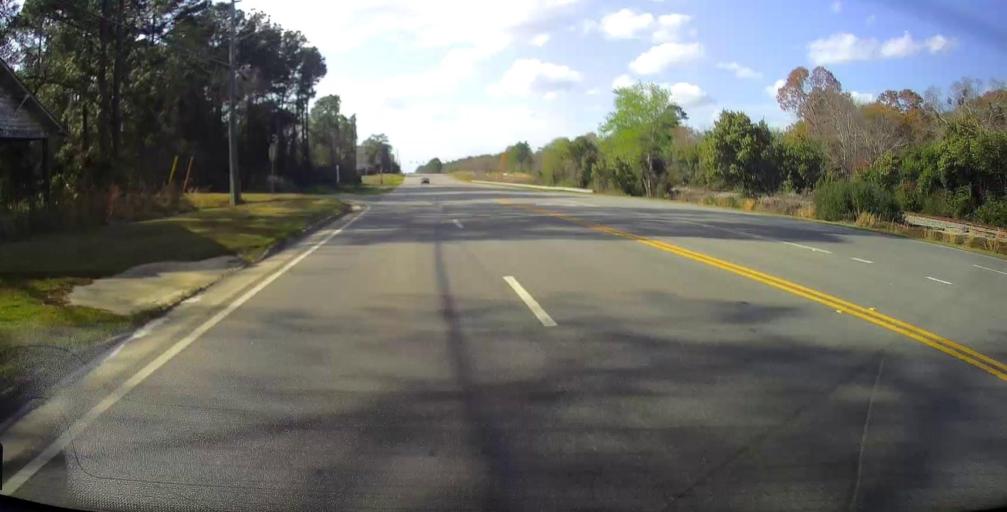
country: US
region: Georgia
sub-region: Telfair County
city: Helena
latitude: 32.0774
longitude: -82.9187
